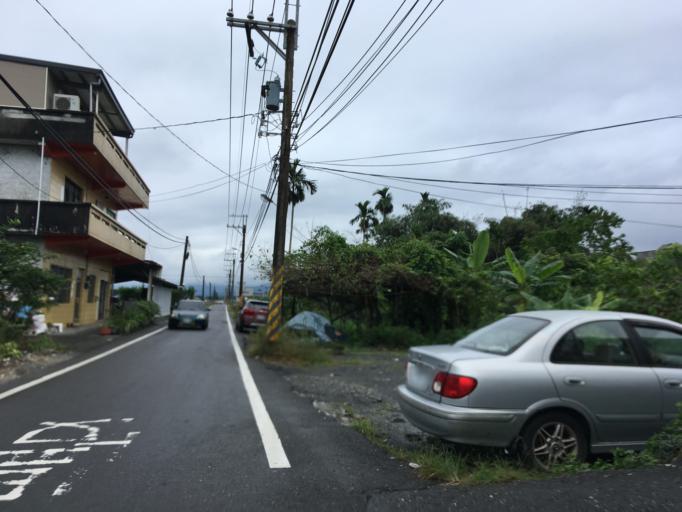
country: TW
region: Taiwan
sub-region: Yilan
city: Yilan
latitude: 24.6660
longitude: 121.7437
